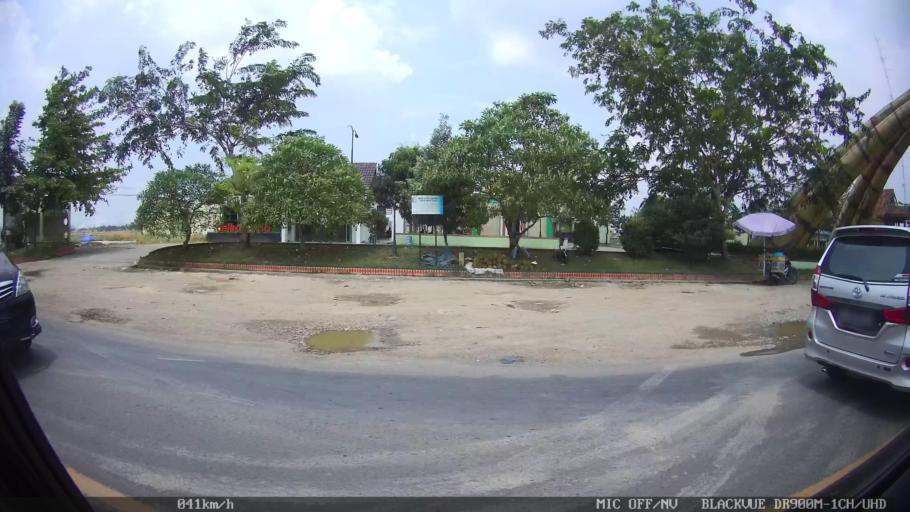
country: ID
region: Lampung
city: Pringsewu
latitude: -5.3723
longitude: 105.0120
